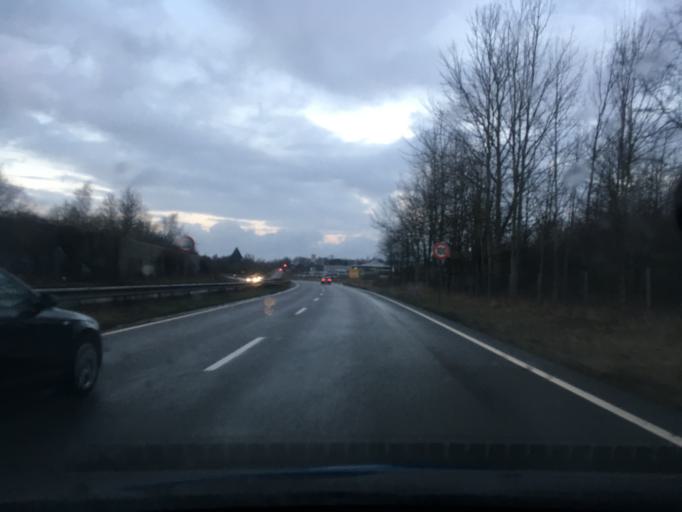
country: DE
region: Lower Saxony
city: Wendisch Evern
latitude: 53.2367
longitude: 10.4553
